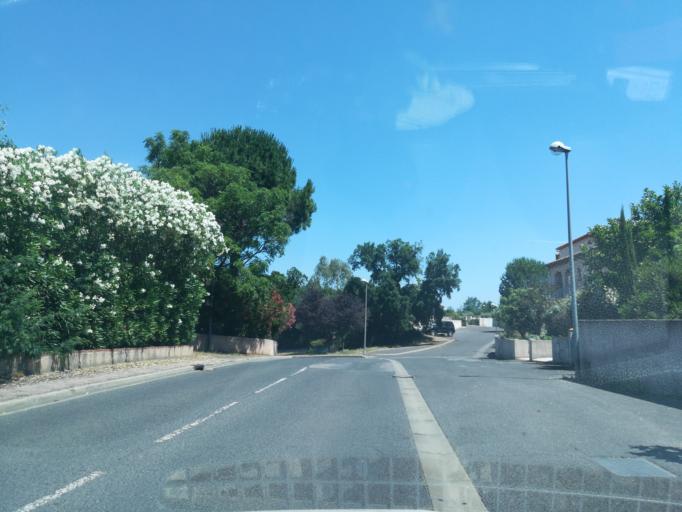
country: FR
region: Languedoc-Roussillon
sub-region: Departement des Pyrenees-Orientales
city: Ceret
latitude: 42.4864
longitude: 2.7448
